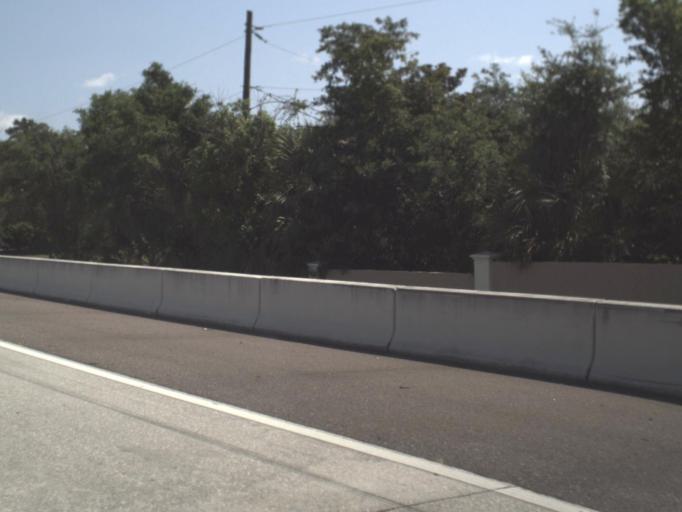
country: US
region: Florida
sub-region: Duval County
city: Jacksonville
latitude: 30.3963
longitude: -81.6679
